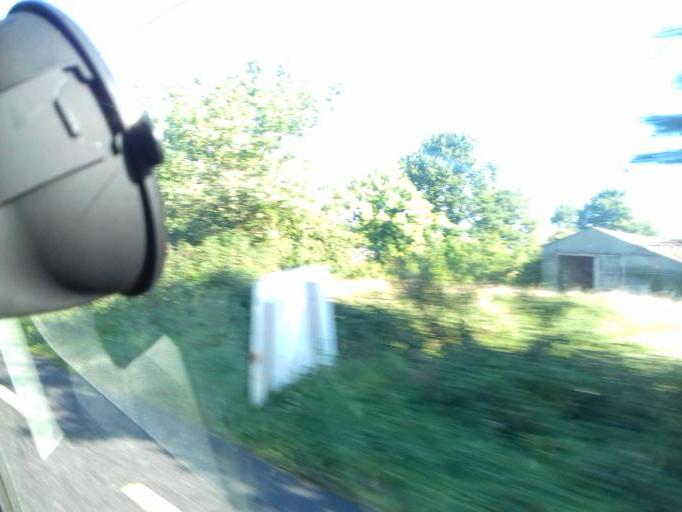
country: IE
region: Leinster
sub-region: Uibh Fhaili
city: Tullamore
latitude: 53.3137
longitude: -7.5060
